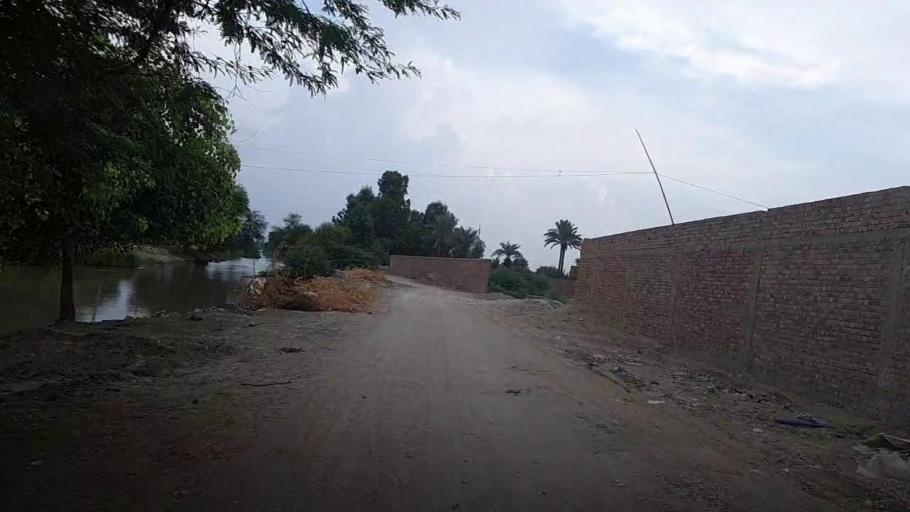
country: PK
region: Sindh
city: Khanpur
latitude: 27.8421
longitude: 69.4158
